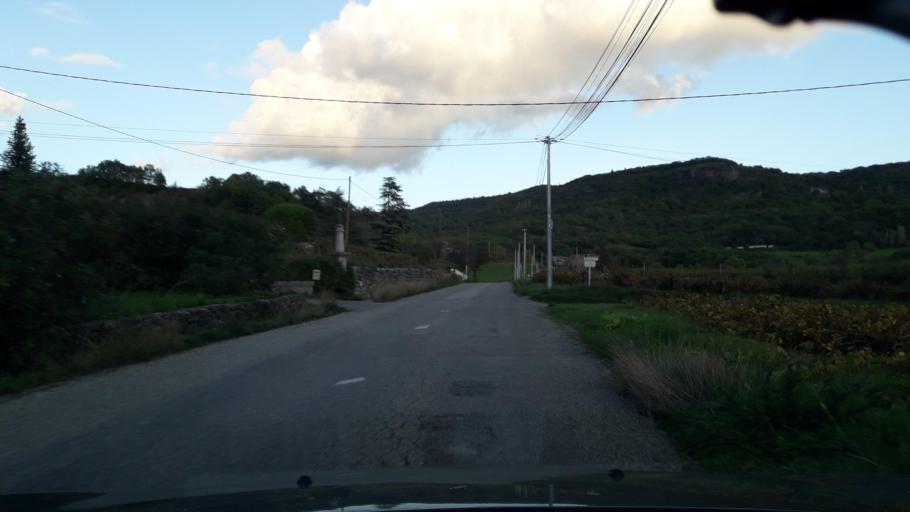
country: FR
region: Rhone-Alpes
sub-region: Departement de l'Ardeche
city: Vesseaux
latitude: 44.6267
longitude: 4.4843
